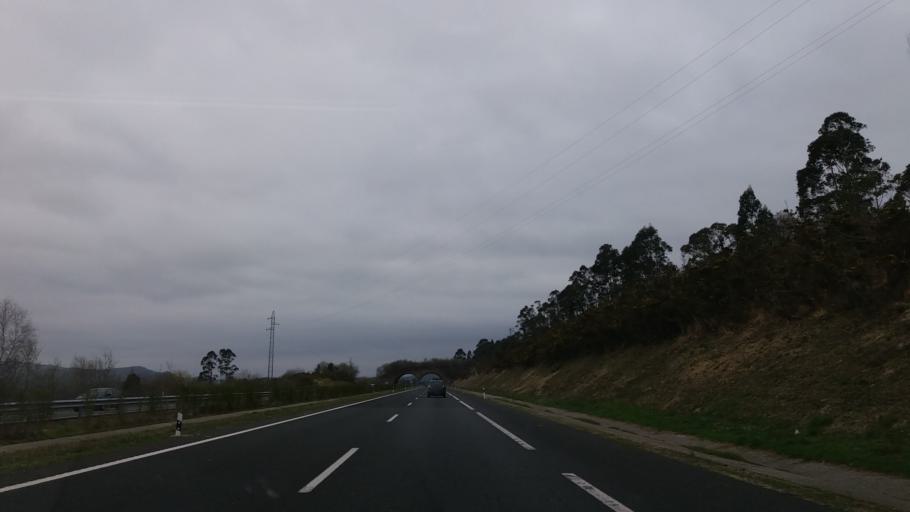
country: ES
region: Cantabria
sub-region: Provincia de Cantabria
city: Cabezon de la Sal
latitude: 43.3223
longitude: -4.2863
